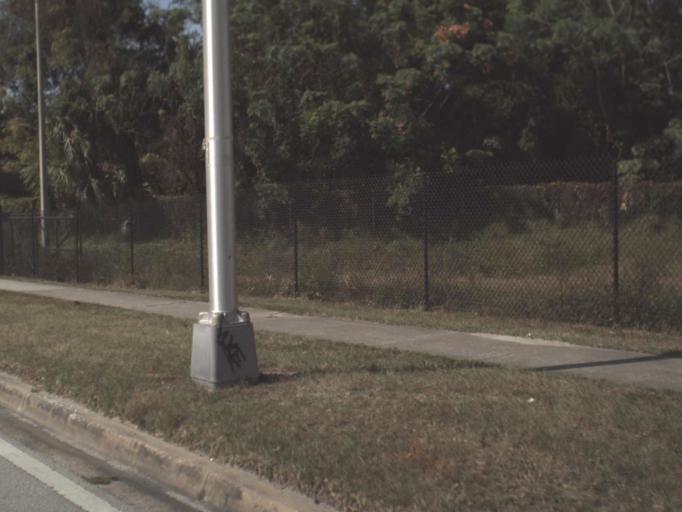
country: US
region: Florida
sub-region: Orange County
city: Orlando
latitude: 28.5312
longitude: -81.3865
